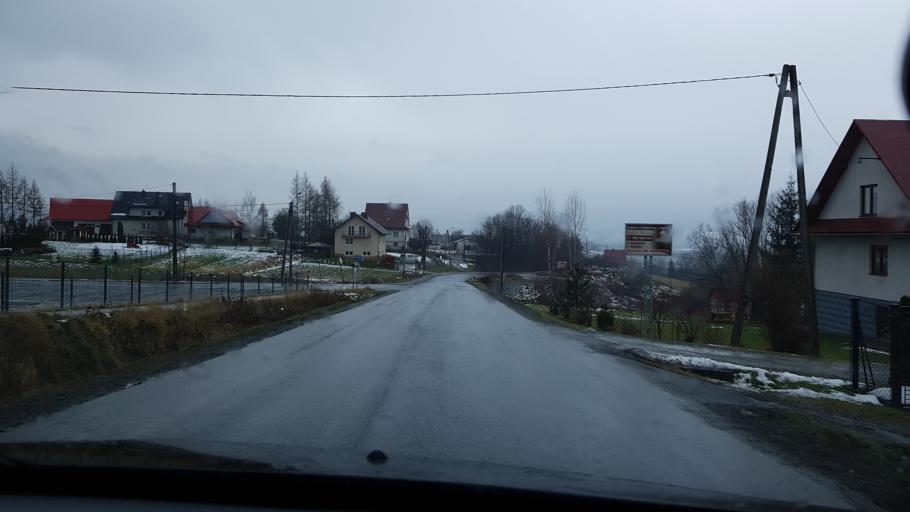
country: PL
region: Lesser Poland Voivodeship
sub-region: Powiat suski
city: Jordanow
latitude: 49.6147
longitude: 19.8472
